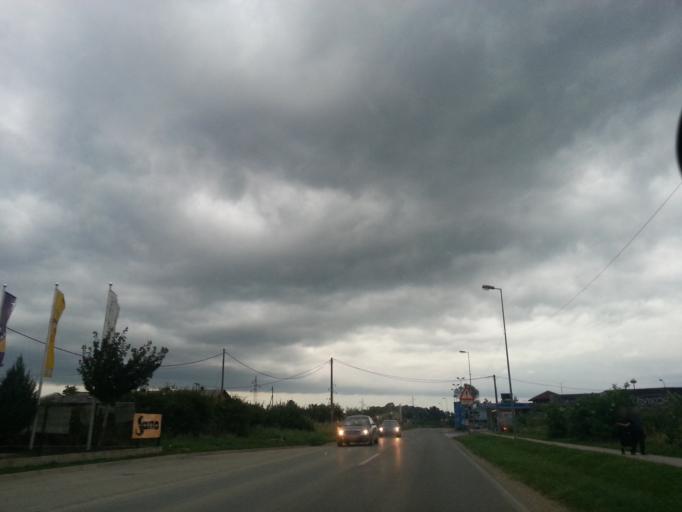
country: BA
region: Brcko
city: Brcko
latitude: 44.8614
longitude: 18.8252
